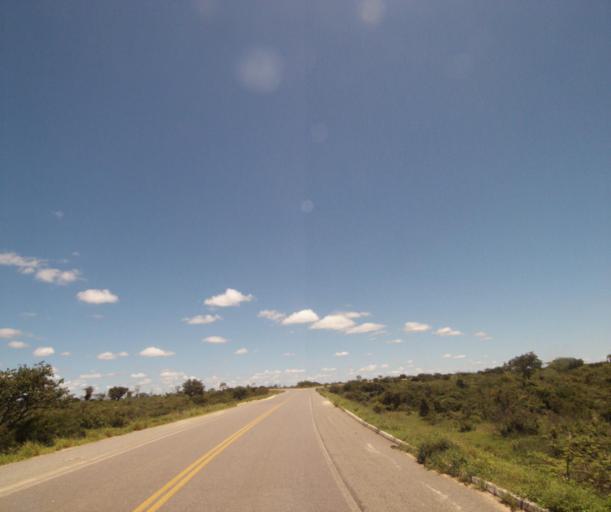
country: BR
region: Bahia
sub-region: Carinhanha
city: Carinhanha
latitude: -14.2896
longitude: -43.7851
